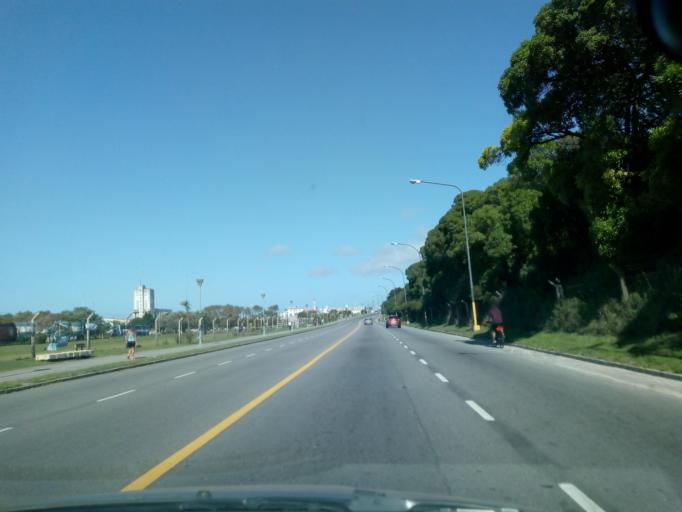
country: AR
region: Buenos Aires
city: Mar del Plata
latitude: -38.0373
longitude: -57.5395
